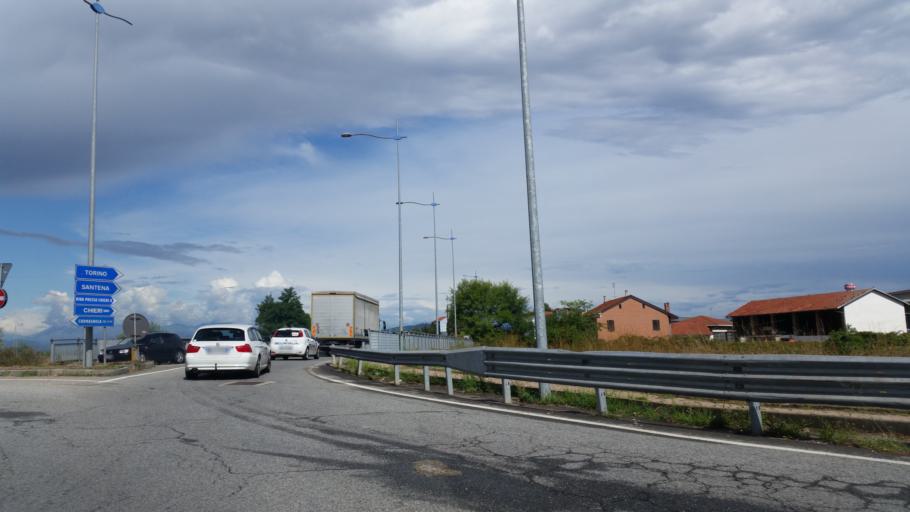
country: IT
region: Piedmont
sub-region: Provincia di Torino
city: Poirino
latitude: 44.9246
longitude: 7.8383
